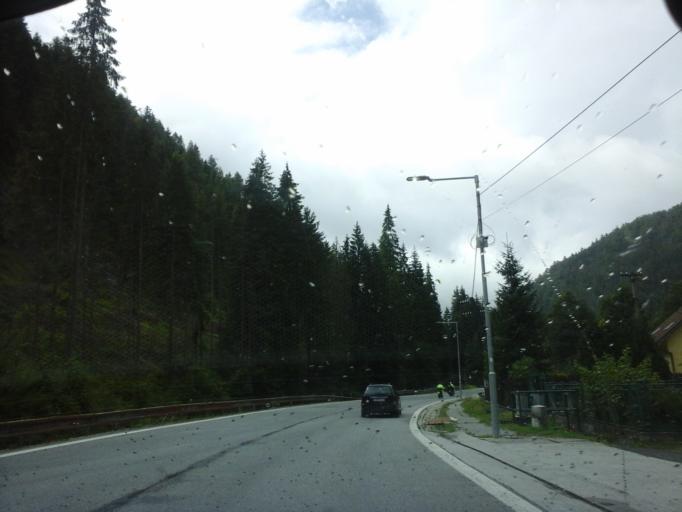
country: SK
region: Kosicky
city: Dobsina
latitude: 48.8684
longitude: 20.3457
